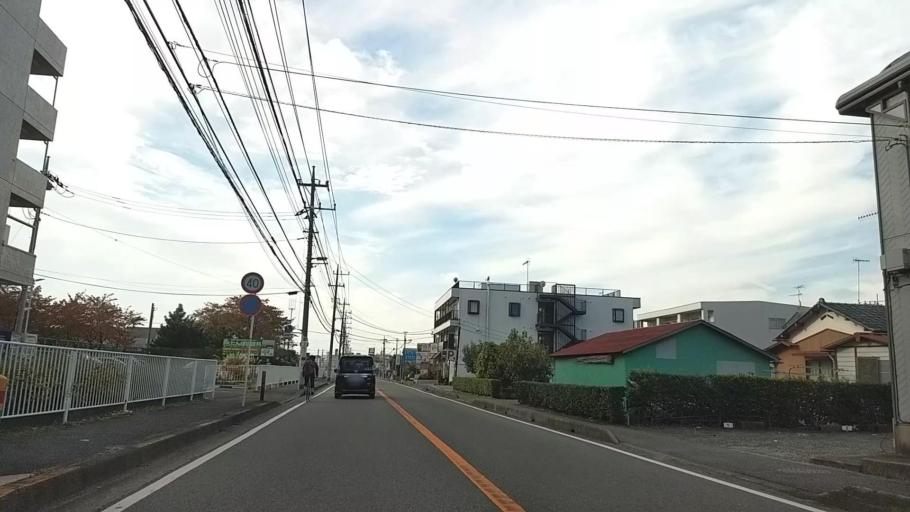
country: JP
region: Kanagawa
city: Zama
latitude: 35.4604
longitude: 139.3870
